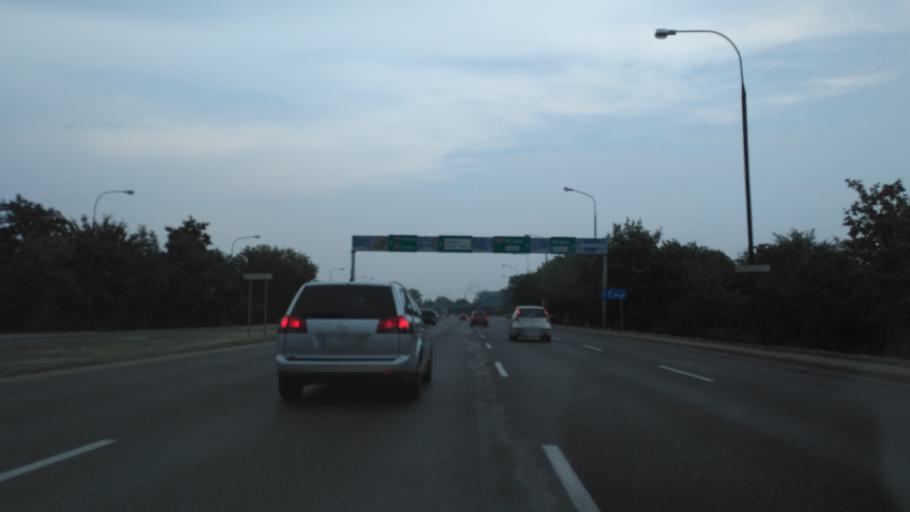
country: PL
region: Lublin Voivodeship
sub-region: Powiat lubelski
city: Lublin
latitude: 51.2505
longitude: 22.5814
